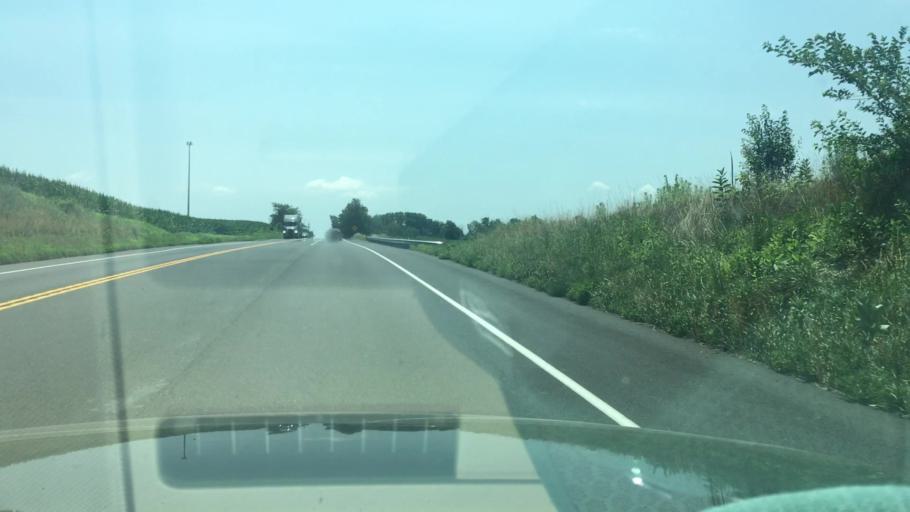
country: US
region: Pennsylvania
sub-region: Carbon County
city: Lehighton
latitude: 40.7053
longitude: -75.7597
